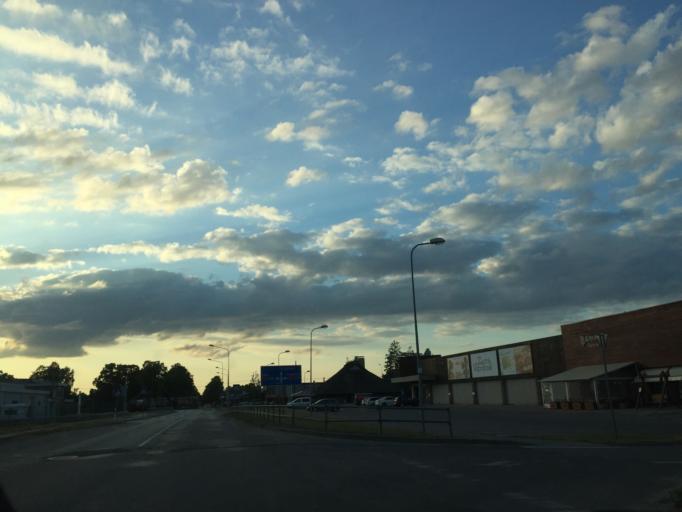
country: LV
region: Sigulda
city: Sigulda
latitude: 57.1438
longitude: 24.8594
